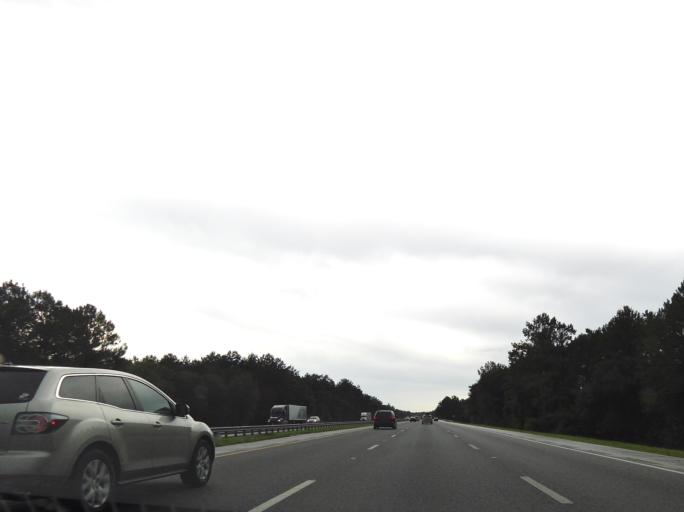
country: US
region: Florida
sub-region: Suwannee County
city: Wellborn
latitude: 30.3382
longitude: -82.8262
